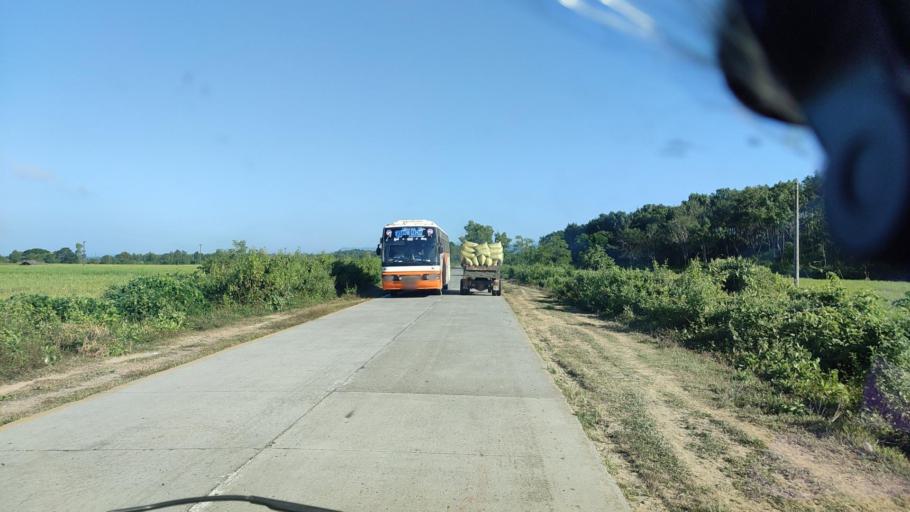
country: MM
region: Rakhine
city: Sittwe
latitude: 20.8014
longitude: 93.0792
